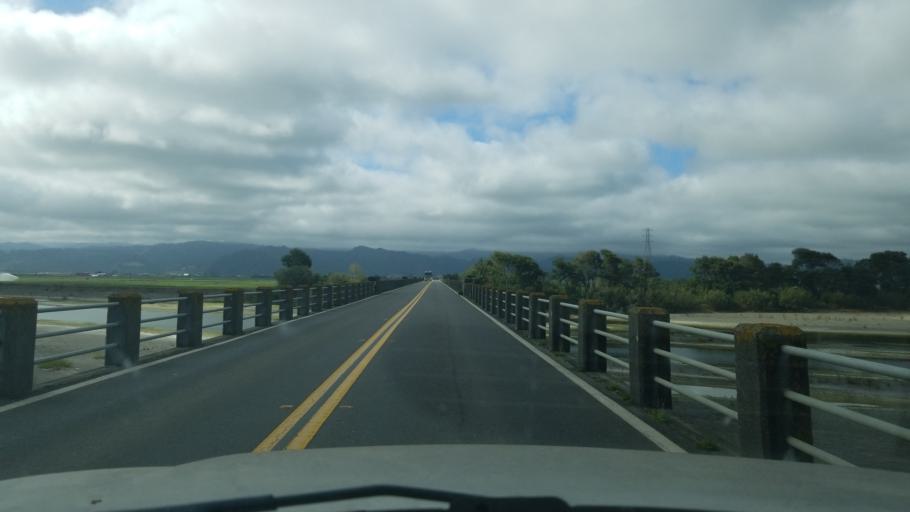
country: US
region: California
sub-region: Humboldt County
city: Fortuna
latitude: 40.6141
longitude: -124.2031
